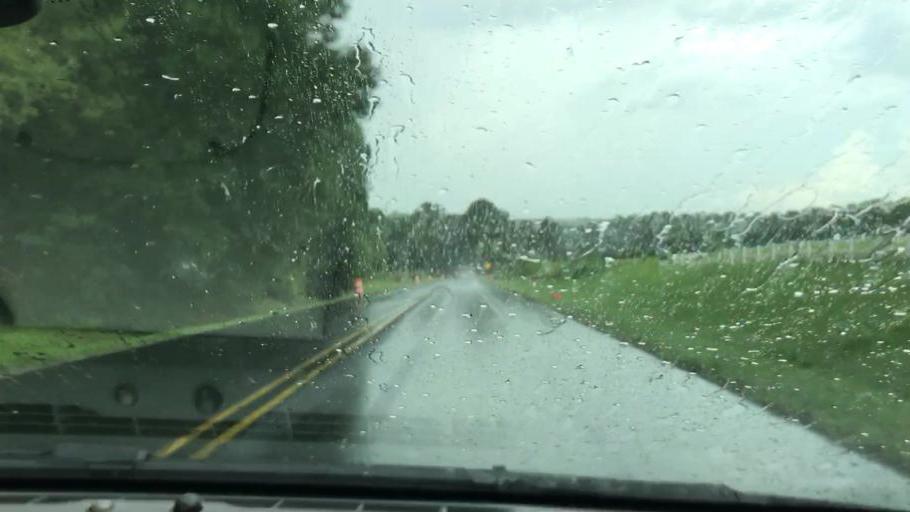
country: US
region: Georgia
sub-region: Clay County
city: Fort Gaines
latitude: 31.5456
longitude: -85.0195
